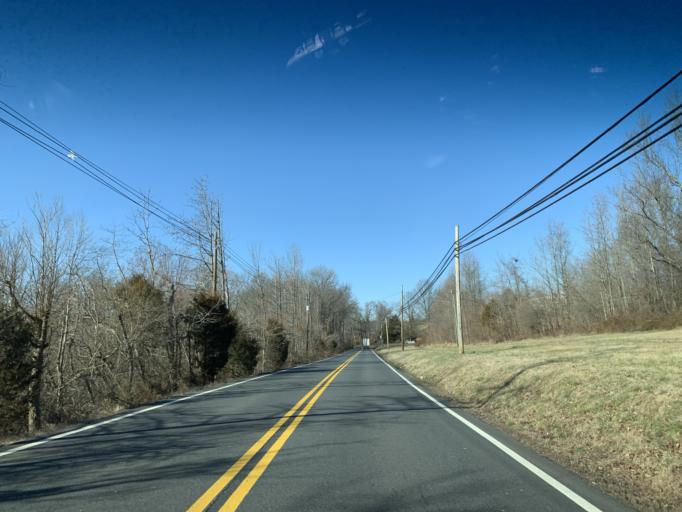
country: US
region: Maryland
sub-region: Cecil County
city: Elkton
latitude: 39.6364
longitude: -75.8639
